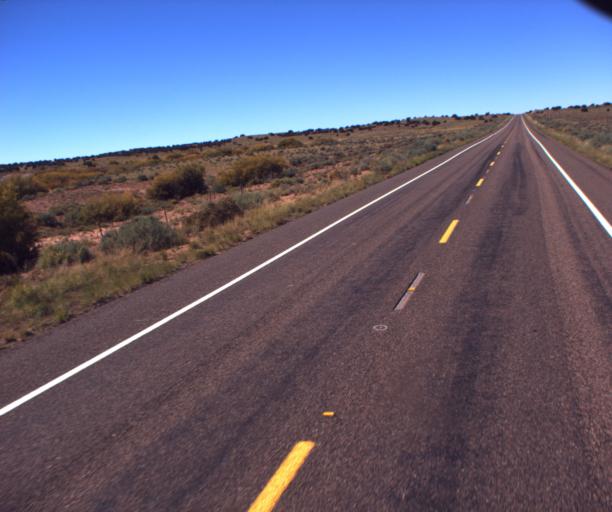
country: US
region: Arizona
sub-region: Apache County
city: Saint Johns
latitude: 34.5925
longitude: -109.6105
